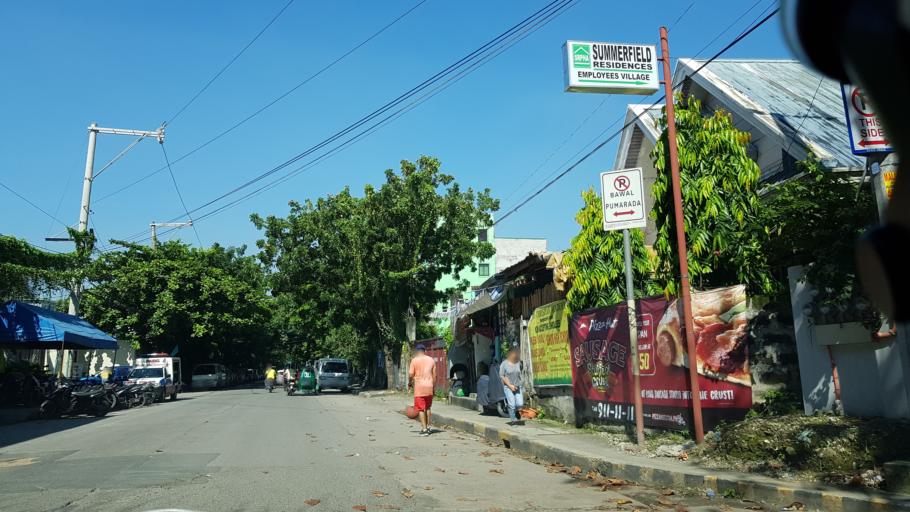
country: PH
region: Calabarzon
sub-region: Province of Rizal
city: Cainta
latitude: 14.5713
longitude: 121.0967
